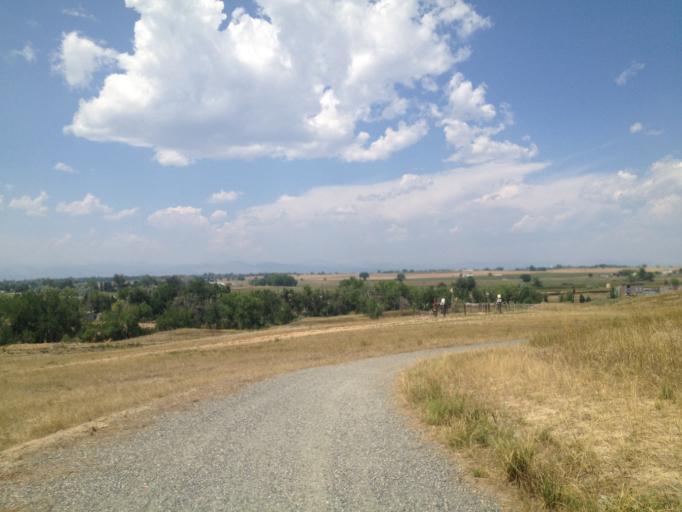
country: US
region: Colorado
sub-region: Boulder County
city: Lafayette
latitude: 39.9979
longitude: -105.0563
